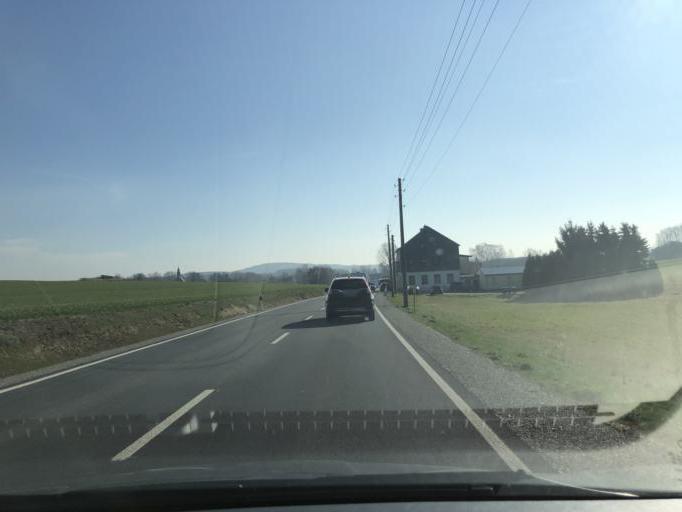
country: DE
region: Saxony
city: Rammenau
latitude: 51.1532
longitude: 14.1246
